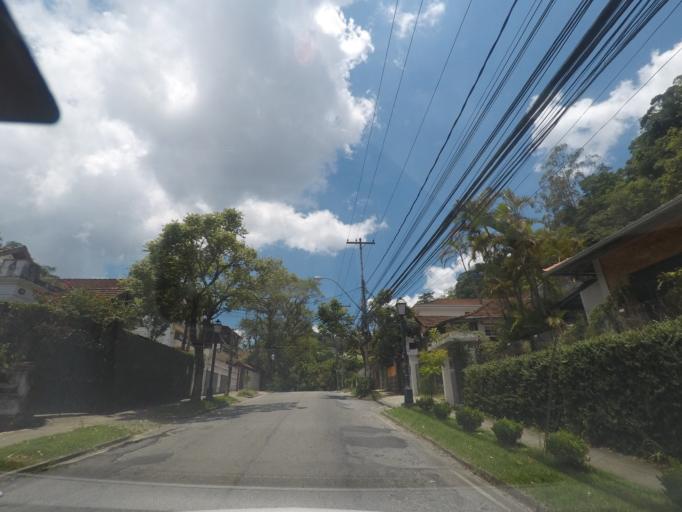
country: BR
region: Rio de Janeiro
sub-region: Petropolis
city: Petropolis
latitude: -22.5053
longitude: -43.1718
